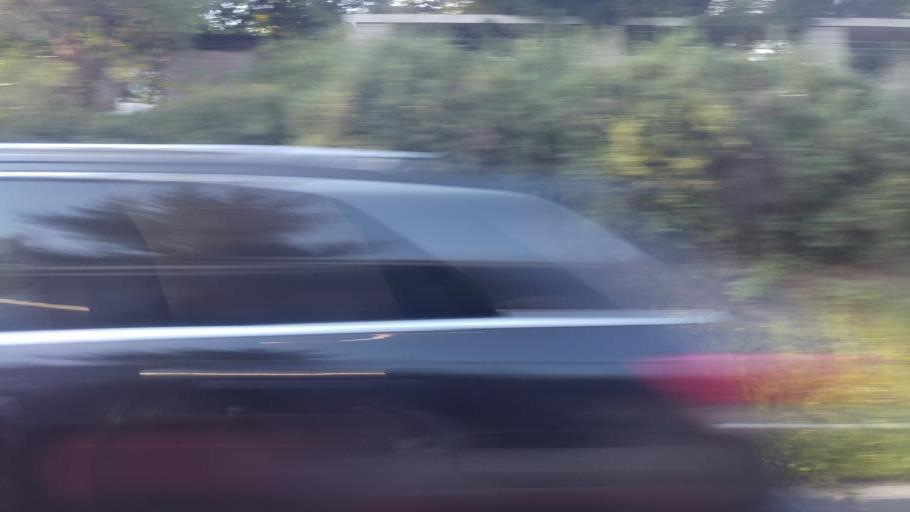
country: CZ
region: Praha
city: Prague
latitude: 50.1174
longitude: 14.4265
